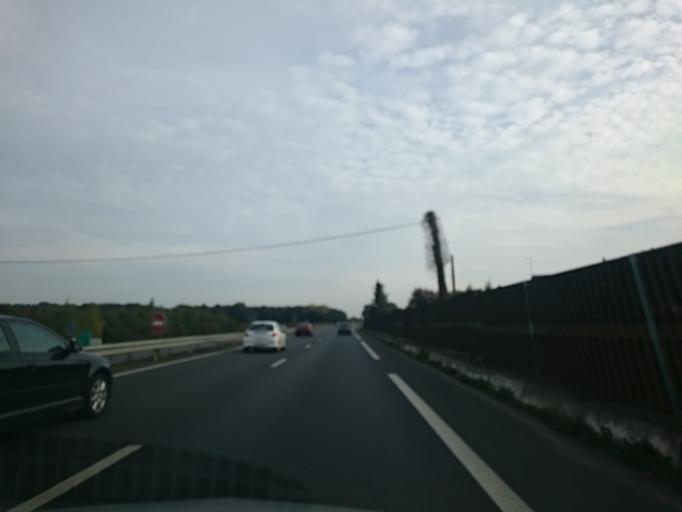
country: FR
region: Brittany
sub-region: Departement d'Ille-et-Vilaine
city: Chantepie
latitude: 48.0698
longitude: -1.6234
